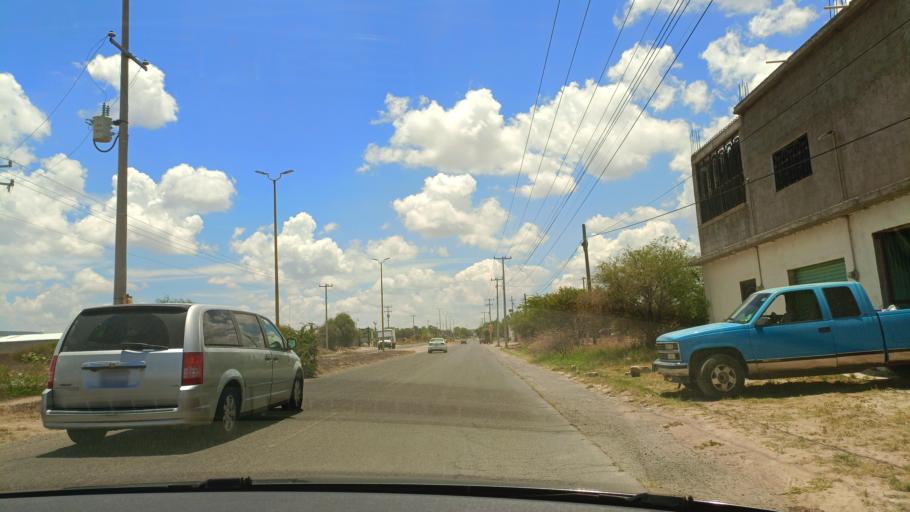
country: MX
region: Guanajuato
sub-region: San Luis de la Paz
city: San Ignacio
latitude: 21.2876
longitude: -100.5491
